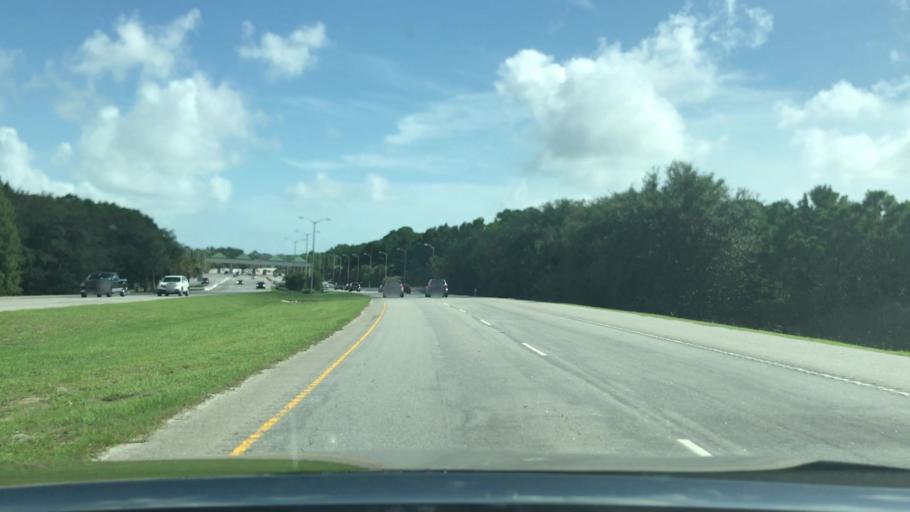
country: US
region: South Carolina
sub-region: Beaufort County
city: Hilton Head Island
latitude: 32.1911
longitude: -80.7654
